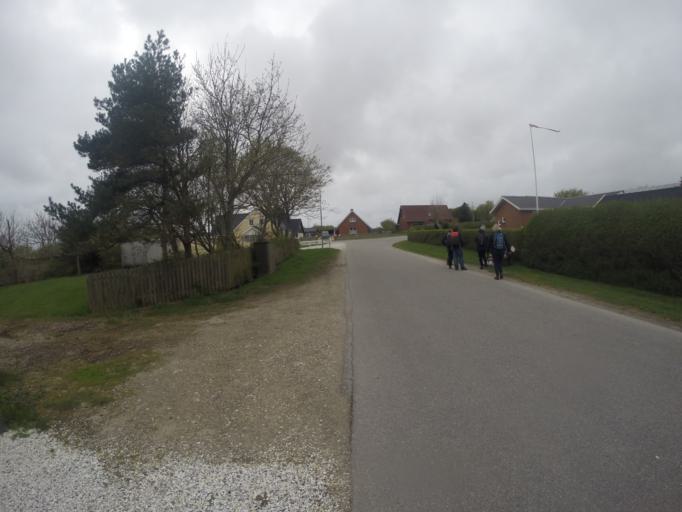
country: DK
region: North Denmark
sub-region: Thisted Kommune
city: Hurup
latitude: 56.9199
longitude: 8.3591
